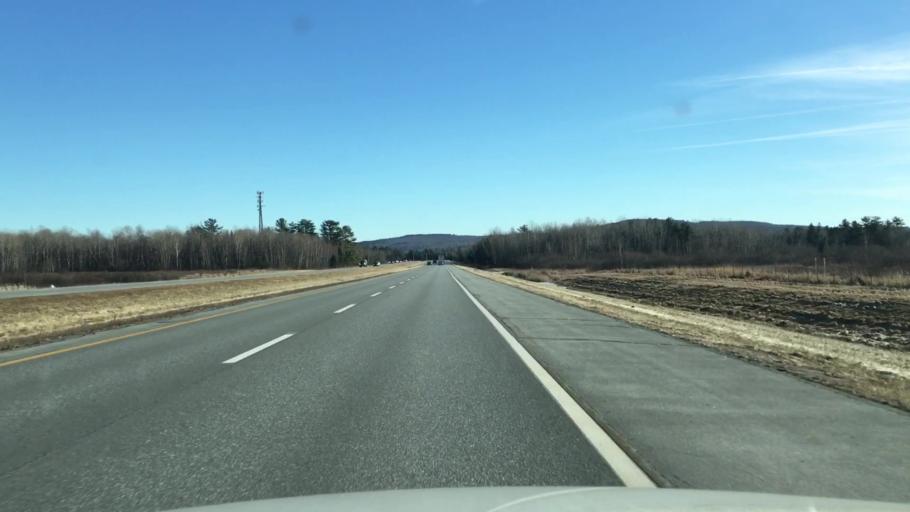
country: US
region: Maine
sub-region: Penobscot County
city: Brewer
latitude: 44.7733
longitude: -68.7451
